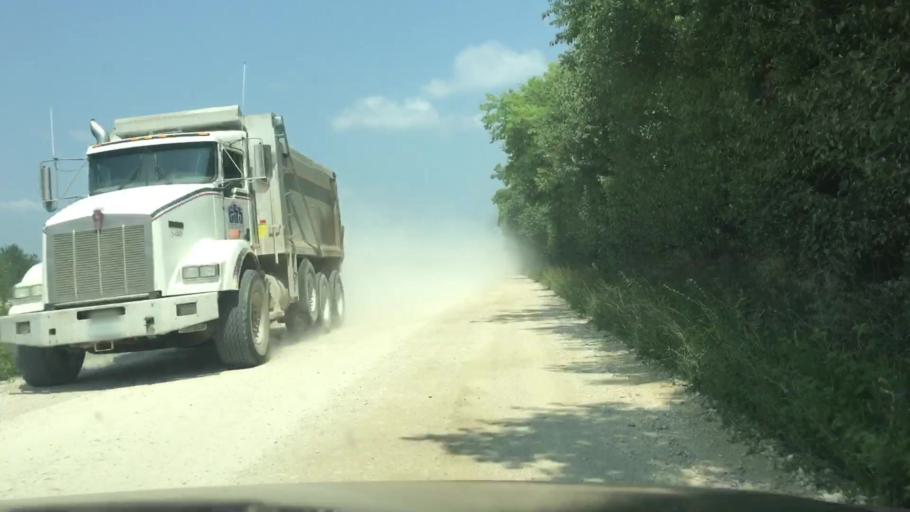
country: US
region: Kansas
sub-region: Allen County
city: Humboldt
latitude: 37.8262
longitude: -95.4093
